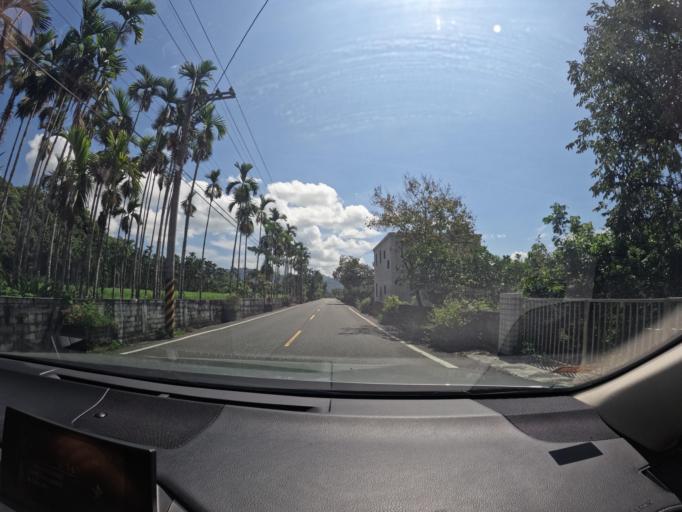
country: TW
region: Taiwan
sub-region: Hualien
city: Hualian
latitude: 23.5817
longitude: 121.3682
